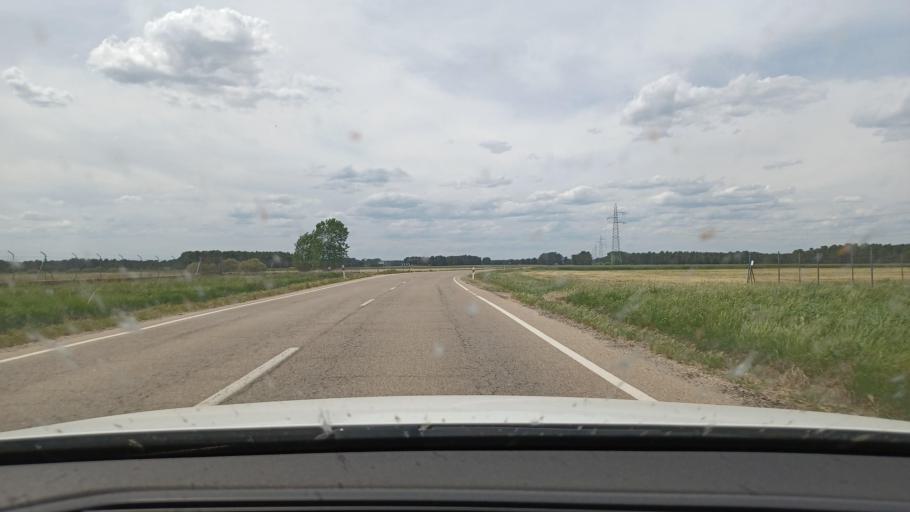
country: ES
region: Castille and Leon
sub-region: Provincia de Segovia
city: Cantalejo
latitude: 41.2695
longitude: -3.9564
